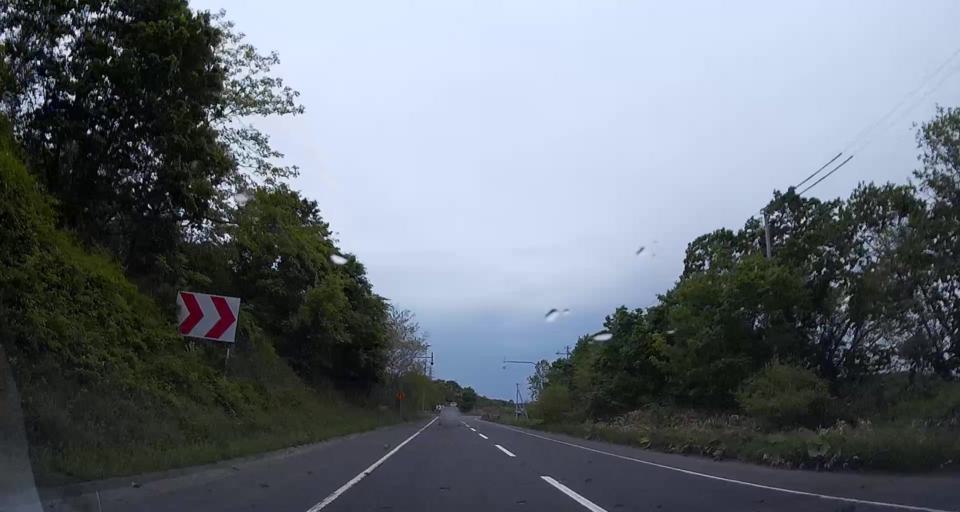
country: JP
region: Hokkaido
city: Chitose
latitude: 42.7007
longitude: 141.7421
